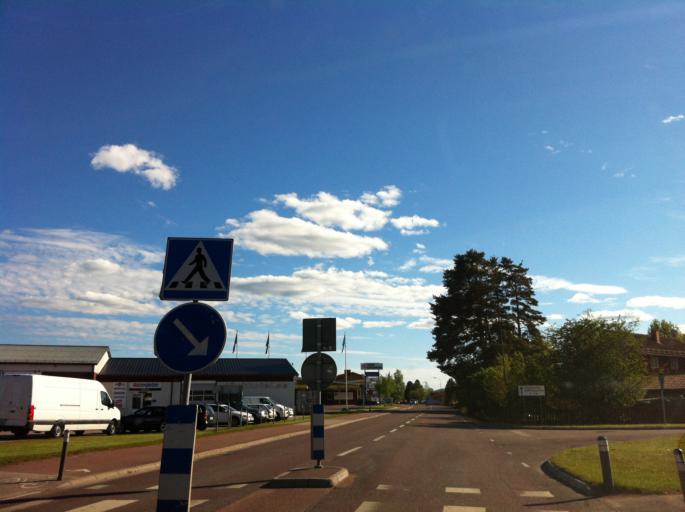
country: SE
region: Dalarna
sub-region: Leksand Municipality
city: Leksand
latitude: 60.7293
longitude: 14.9981
